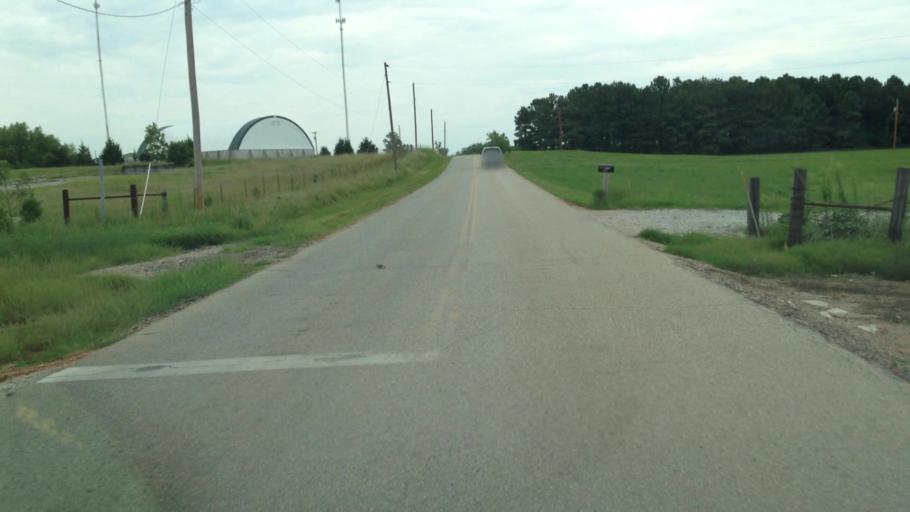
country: US
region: Oklahoma
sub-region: Craig County
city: Vinita
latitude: 36.6339
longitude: -95.1256
